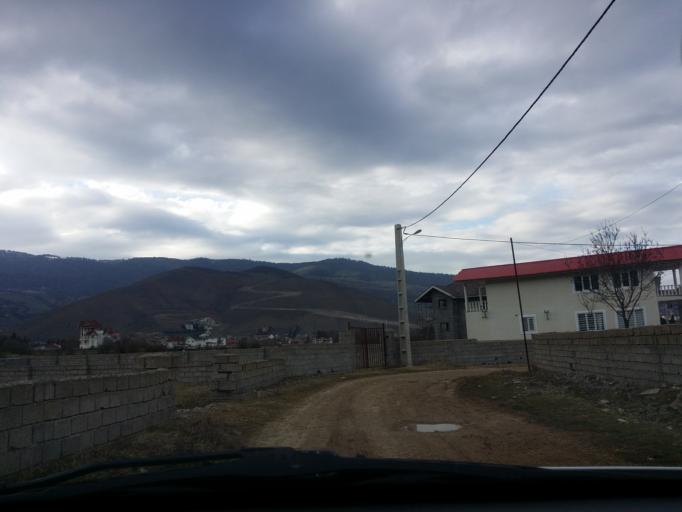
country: IR
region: Mazandaran
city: `Abbasabad
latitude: 36.5012
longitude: 51.1718
